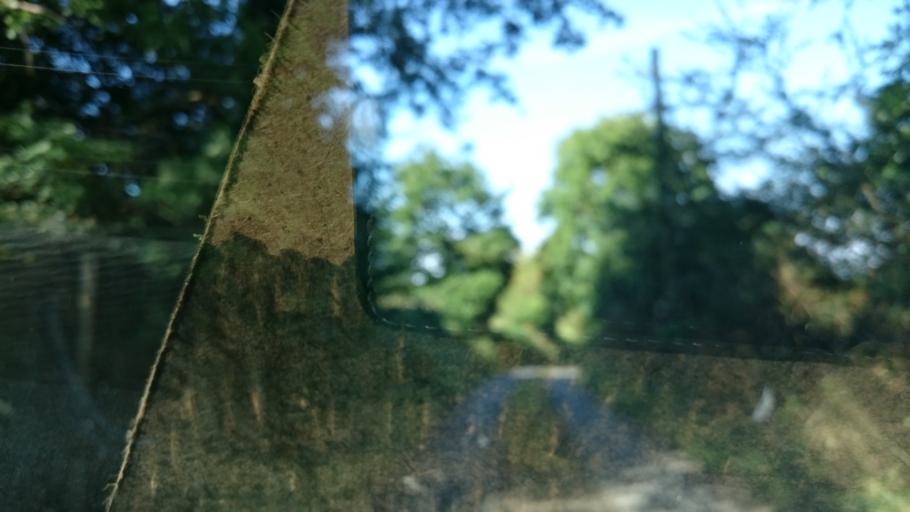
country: IE
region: Leinster
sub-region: Kilkenny
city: Graiguenamanagh
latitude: 52.5242
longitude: -6.9628
